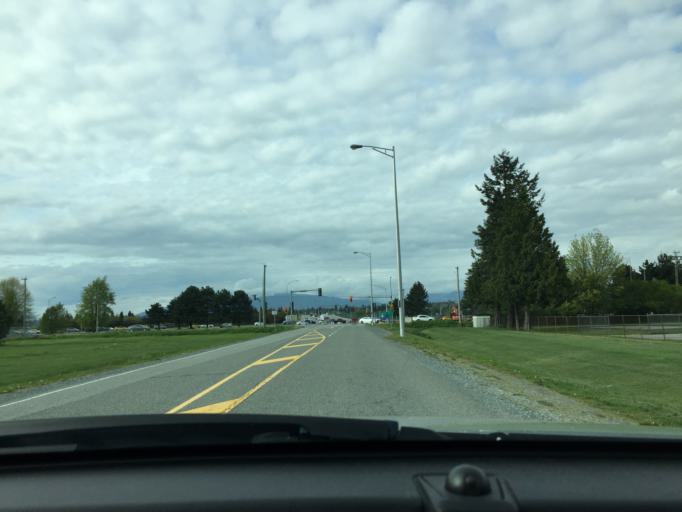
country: CA
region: British Columbia
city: Richmond
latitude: 49.1909
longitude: -123.1508
